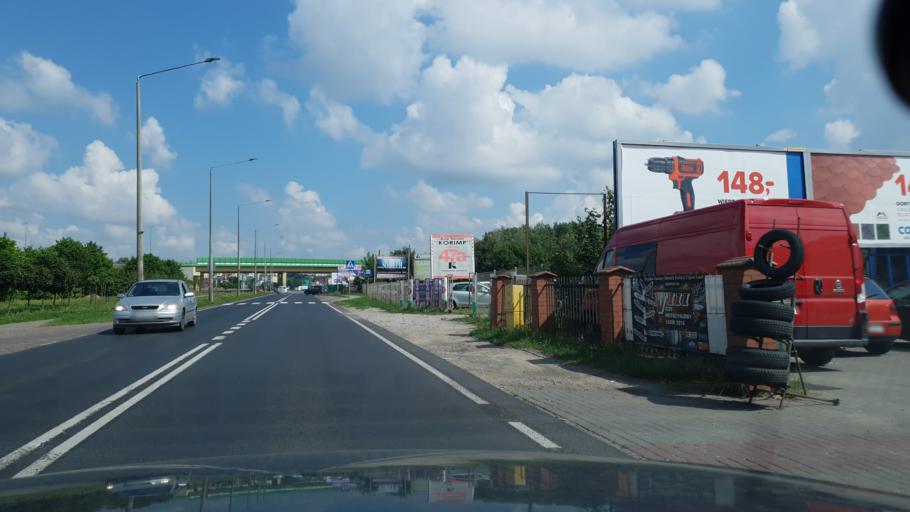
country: PL
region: Kujawsko-Pomorskie
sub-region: Grudziadz
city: Grudziadz
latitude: 53.4437
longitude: 18.7278
